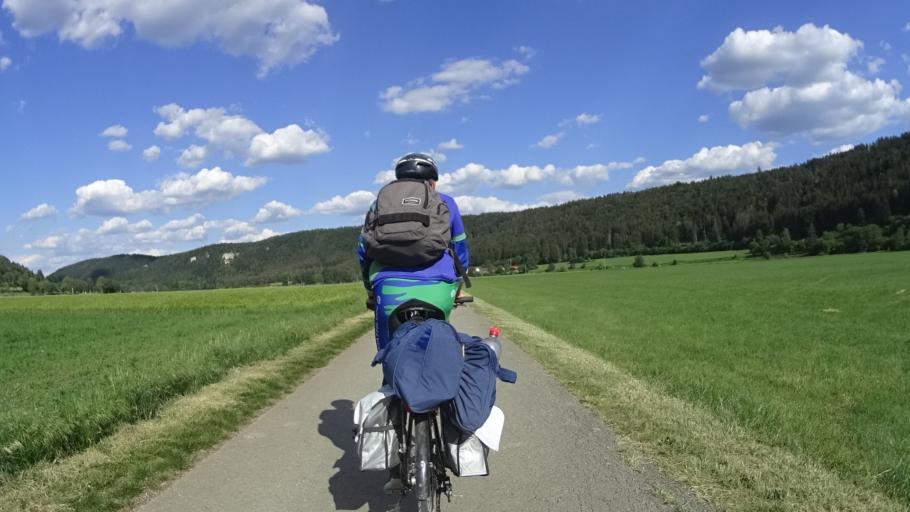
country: DE
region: Bavaria
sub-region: Upper Palatinate
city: Dietfurt
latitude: 49.0123
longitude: 11.5377
